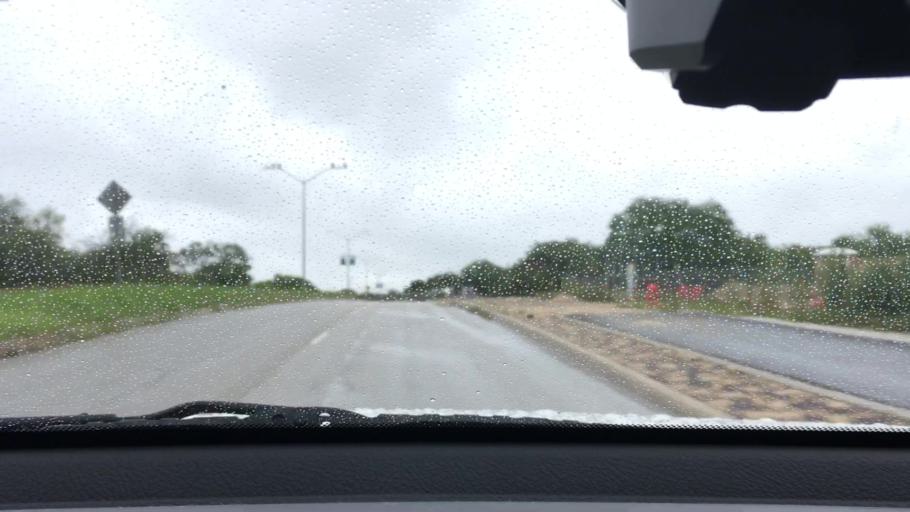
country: US
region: Texas
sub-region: Bexar County
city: Leon Valley
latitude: 29.5241
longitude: -98.5909
